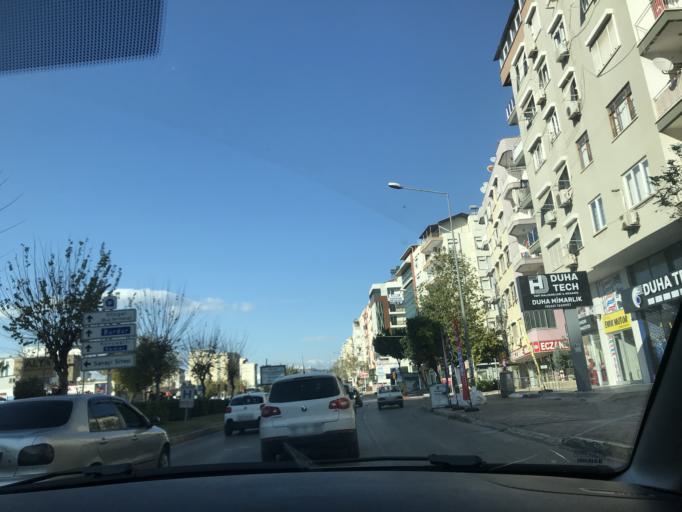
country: TR
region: Antalya
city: Antalya
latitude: 36.9065
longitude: 30.6999
